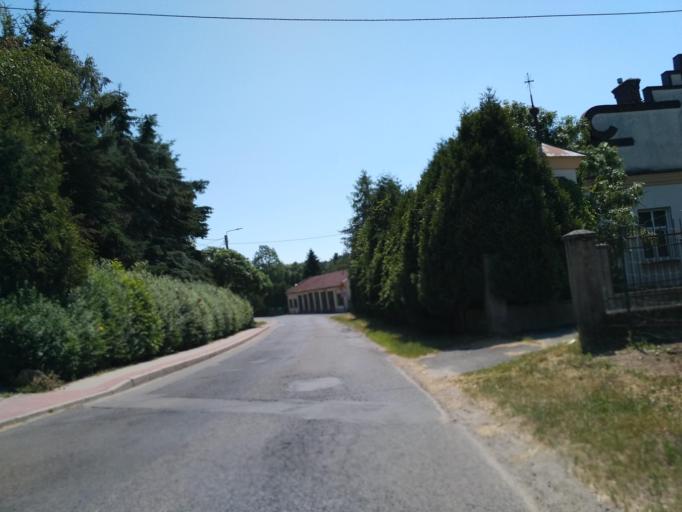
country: PL
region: Subcarpathian Voivodeship
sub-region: Krosno
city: Krosno
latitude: 49.6966
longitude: 21.7847
